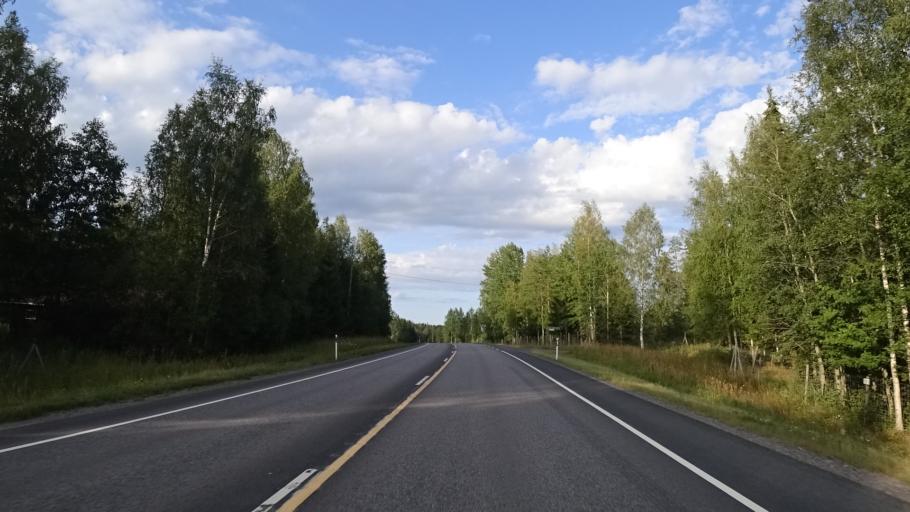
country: FI
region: South Karelia
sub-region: Imatra
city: Rautjaervi
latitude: 61.4052
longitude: 29.3003
